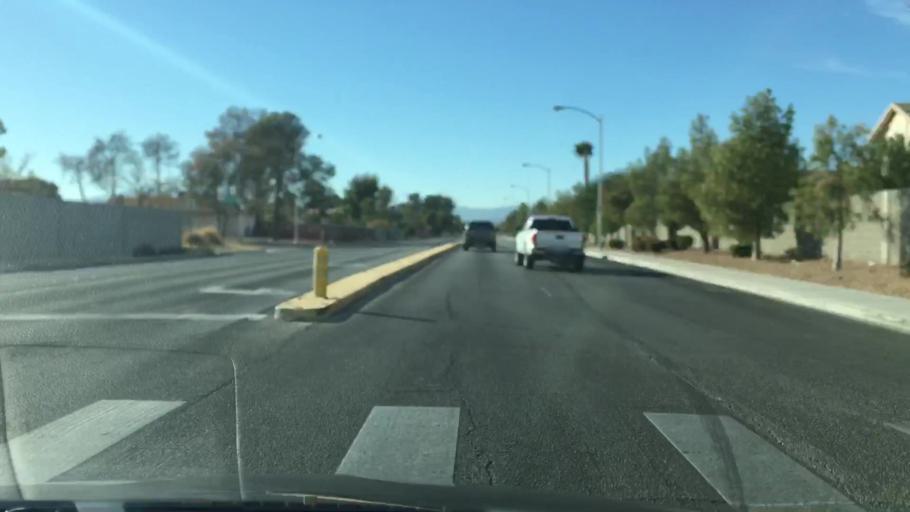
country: US
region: Nevada
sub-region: Clark County
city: Whitney
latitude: 36.0496
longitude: -115.1184
